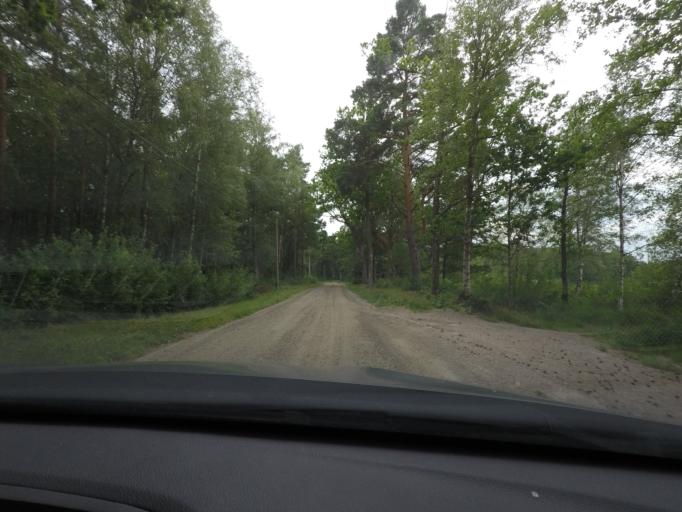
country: SE
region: Skane
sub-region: Osby Kommun
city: Osby
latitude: 56.3565
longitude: 13.9951
